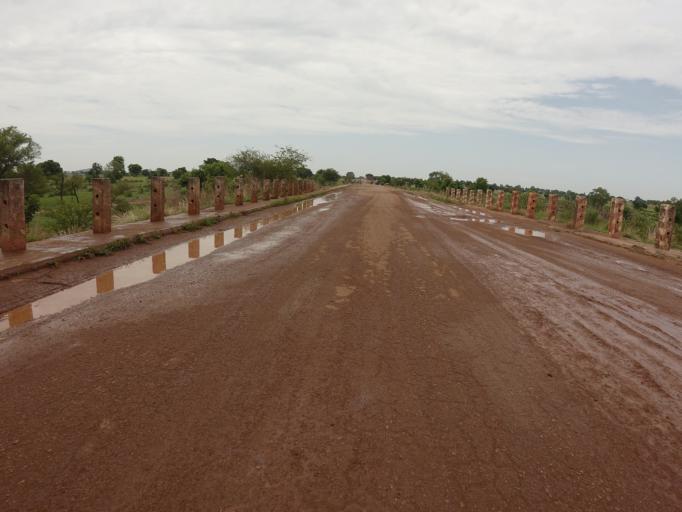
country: GH
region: Upper East
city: Bawku
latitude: 11.0025
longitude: -0.3819
